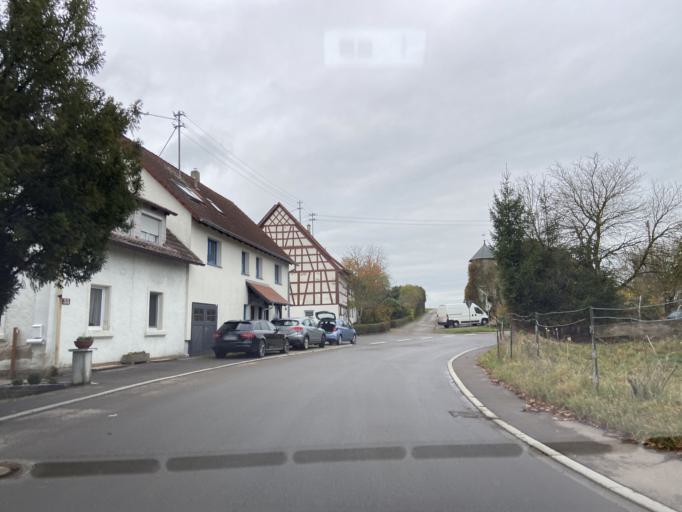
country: DE
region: Baden-Wuerttemberg
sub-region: Tuebingen Region
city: Wald
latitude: 47.9673
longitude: 9.1754
